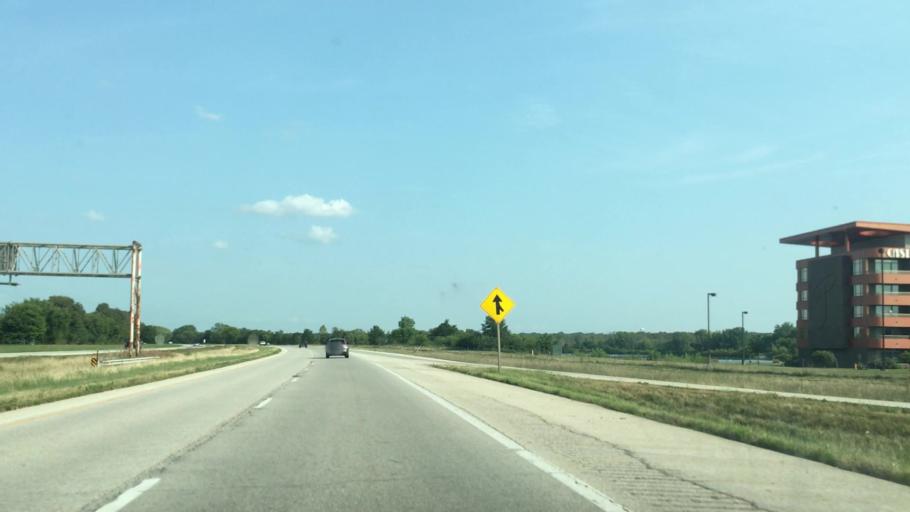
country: US
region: Illinois
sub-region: Rock Island County
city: Milan
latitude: 41.4613
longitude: -90.6123
